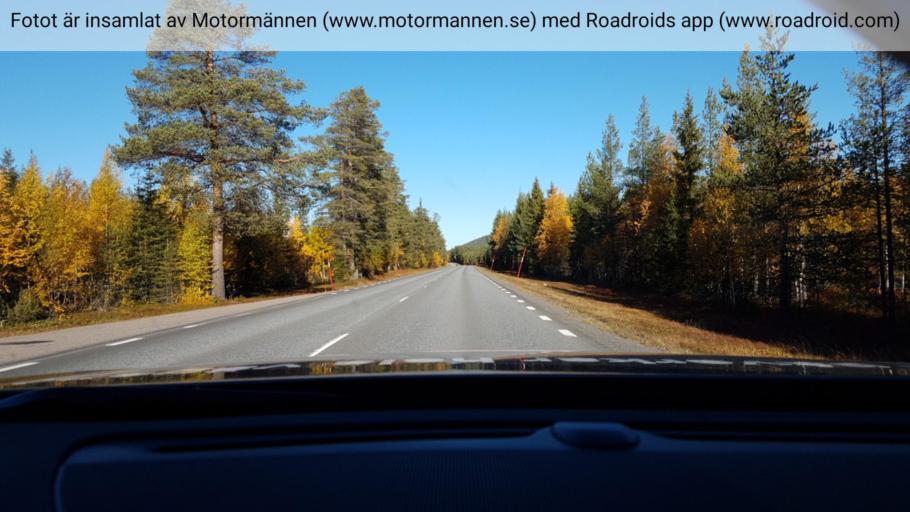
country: SE
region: Norrbotten
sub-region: Arvidsjaurs Kommun
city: Arvidsjaur
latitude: 65.5073
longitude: 19.2868
